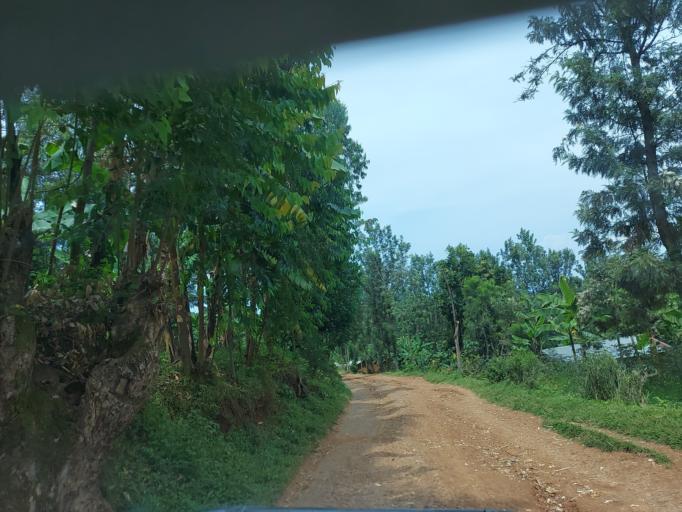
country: CD
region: South Kivu
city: Bukavu
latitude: -2.2359
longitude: 28.8478
